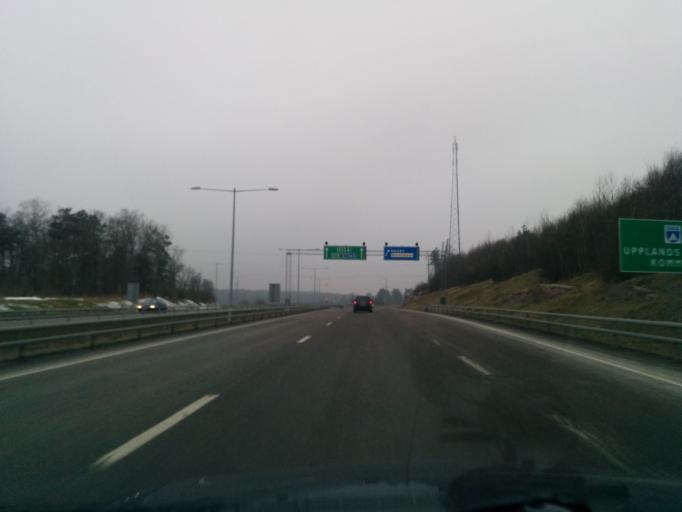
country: SE
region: Stockholm
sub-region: Sollentuna Kommun
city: Sollentuna
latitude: 59.4746
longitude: 18.0033
